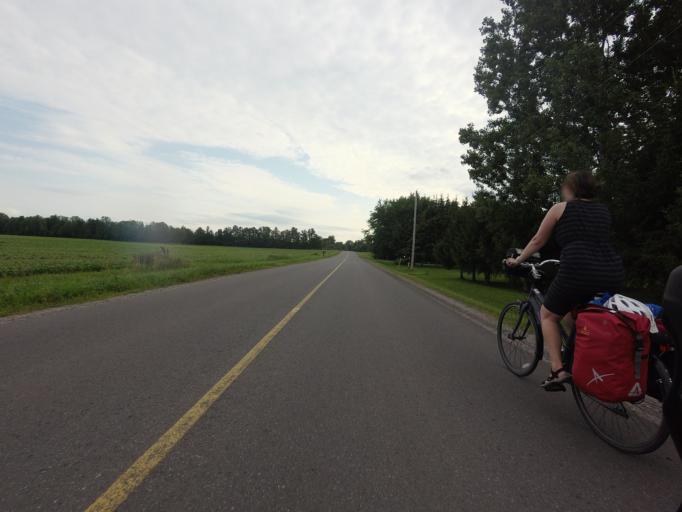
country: CA
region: Ontario
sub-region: Lanark County
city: Smiths Falls
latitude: 44.9963
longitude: -75.7602
